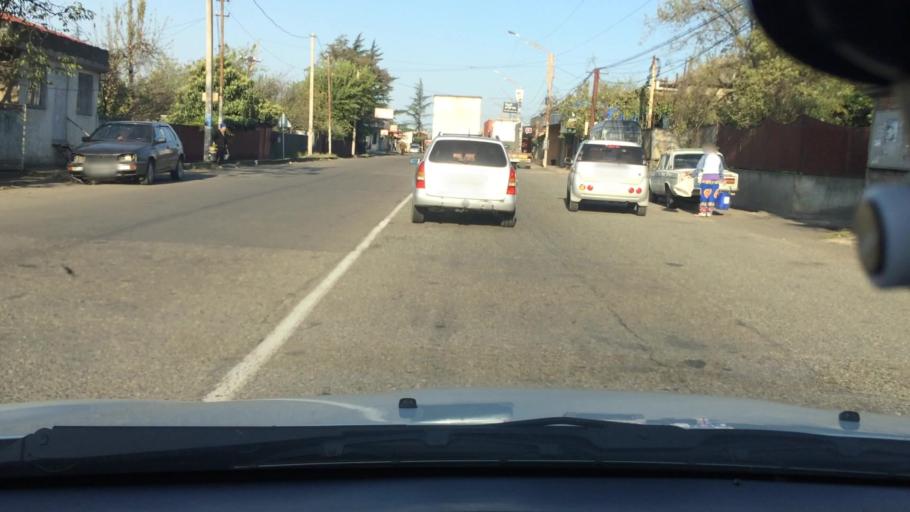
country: GE
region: Imereti
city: Zestap'oni
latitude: 42.1109
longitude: 43.0422
